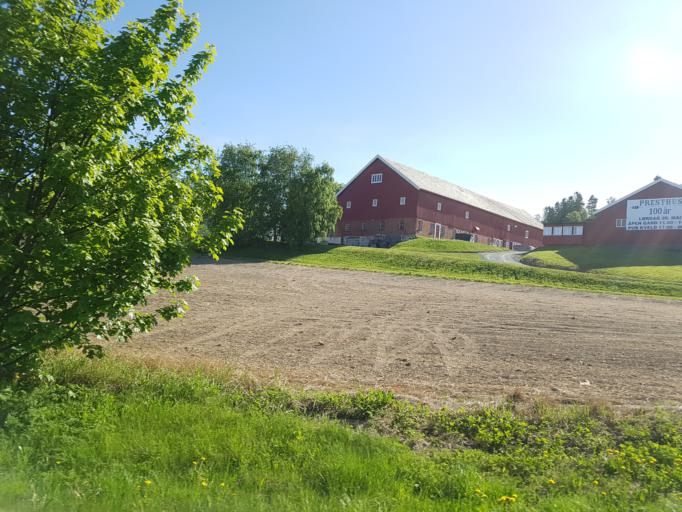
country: NO
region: Sor-Trondelag
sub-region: Trondheim
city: Trondheim
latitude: 63.4247
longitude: 10.5155
